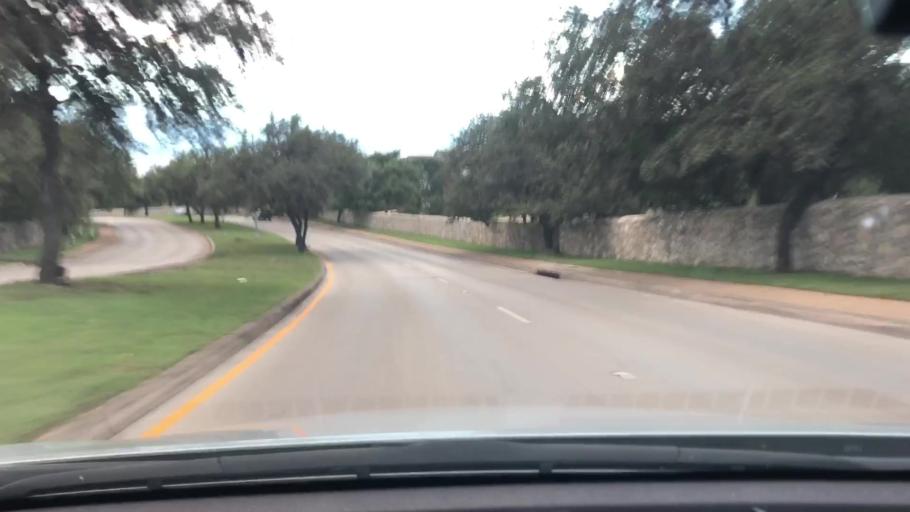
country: US
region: Texas
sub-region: Bexar County
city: Shavano Park
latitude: 29.5981
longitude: -98.5342
